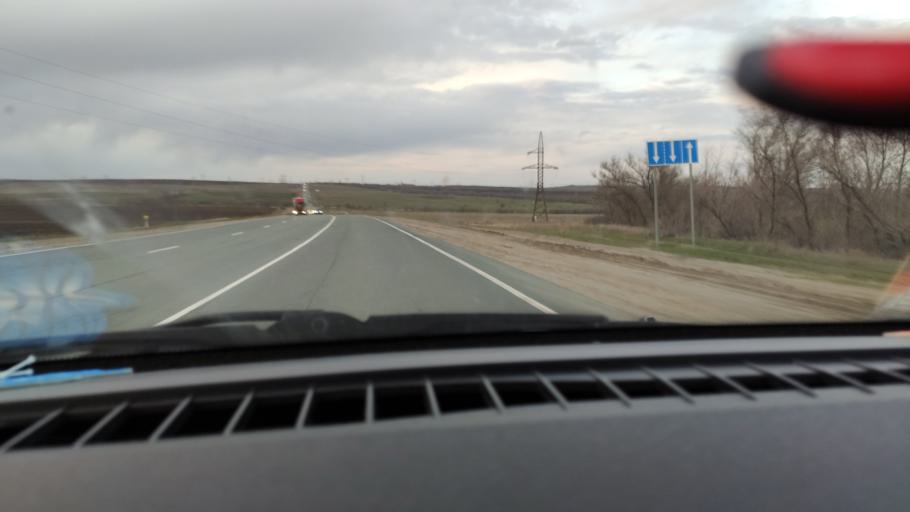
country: RU
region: Saratov
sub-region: Saratovskiy Rayon
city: Saratov
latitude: 51.7523
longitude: 46.0616
